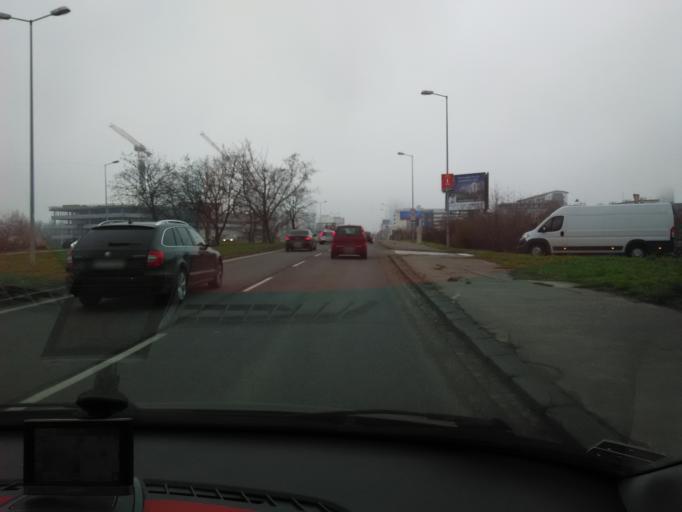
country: SK
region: Bratislavsky
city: Bratislava
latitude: 48.1572
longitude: 17.1443
